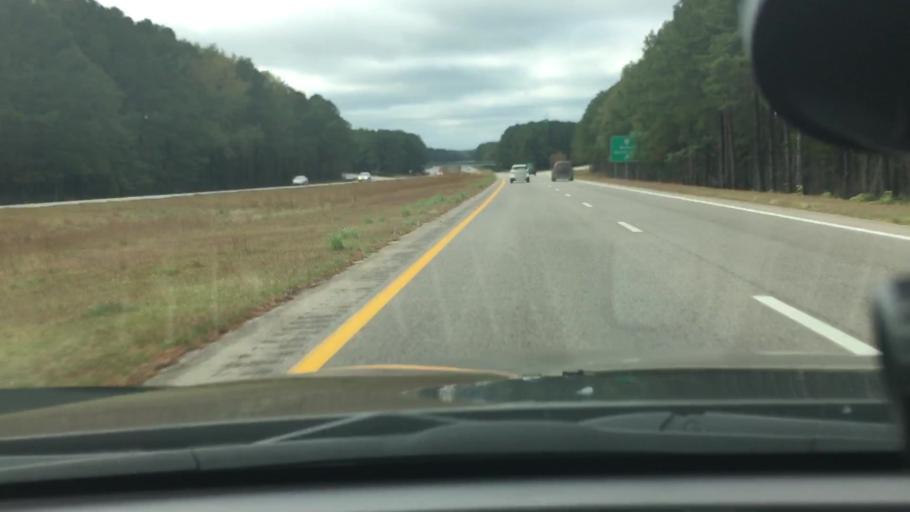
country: US
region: North Carolina
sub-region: Nash County
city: Spring Hope
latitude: 35.7874
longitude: -78.1100
